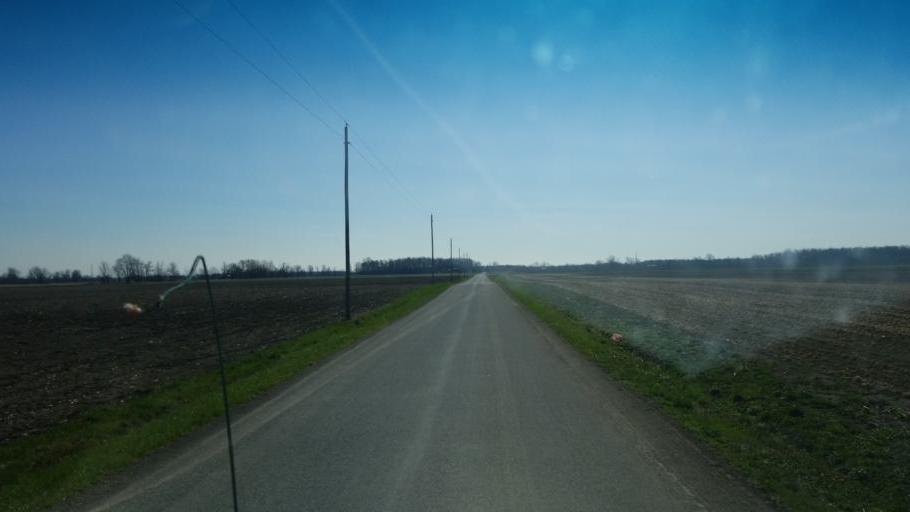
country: US
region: Ohio
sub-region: Hardin County
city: Forest
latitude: 40.7017
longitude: -83.5188
